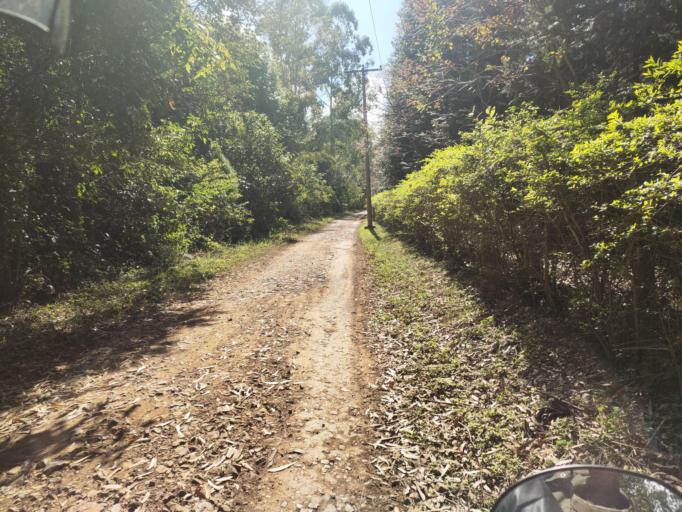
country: MM
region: Mandalay
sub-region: Pyin Oo Lwin District
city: Pyin Oo Lwin
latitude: 21.9854
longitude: 96.4664
